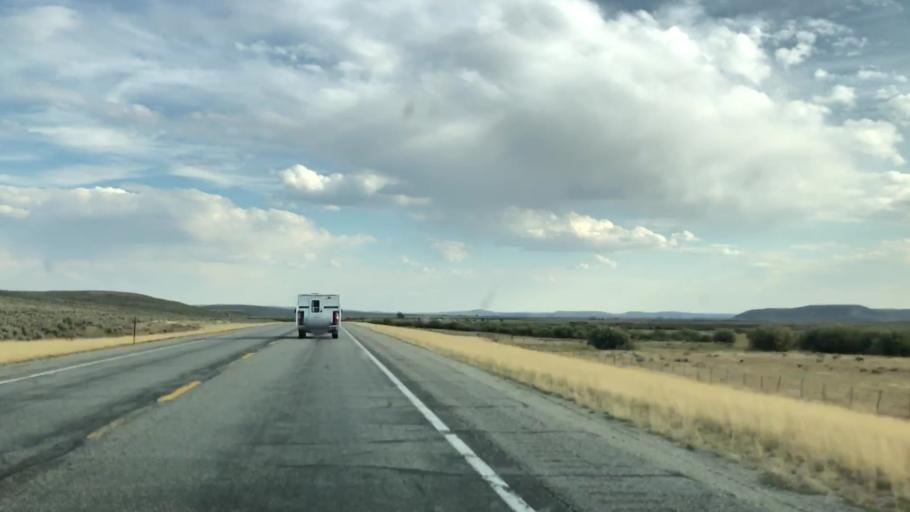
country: US
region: Wyoming
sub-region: Sublette County
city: Pinedale
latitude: 43.0263
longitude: -110.1249
